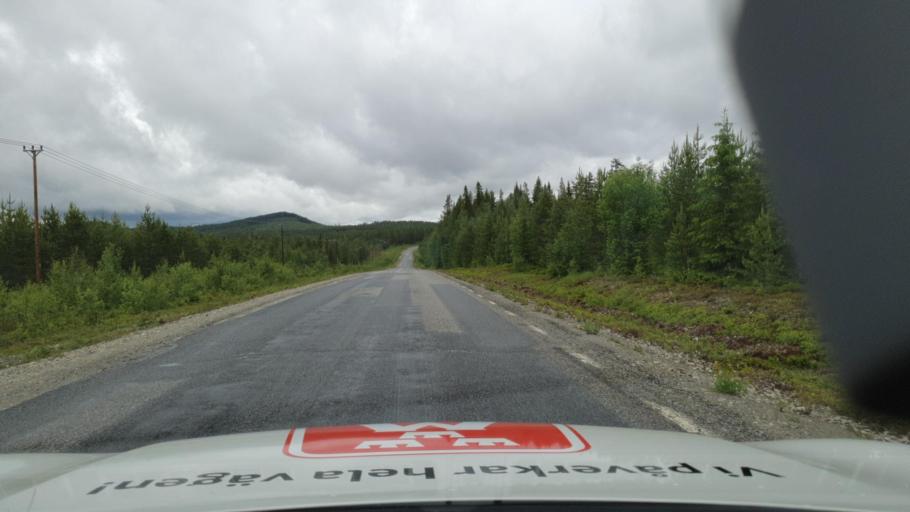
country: SE
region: Vaesterbotten
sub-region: Dorotea Kommun
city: Dorotea
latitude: 64.1514
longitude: 16.6503
